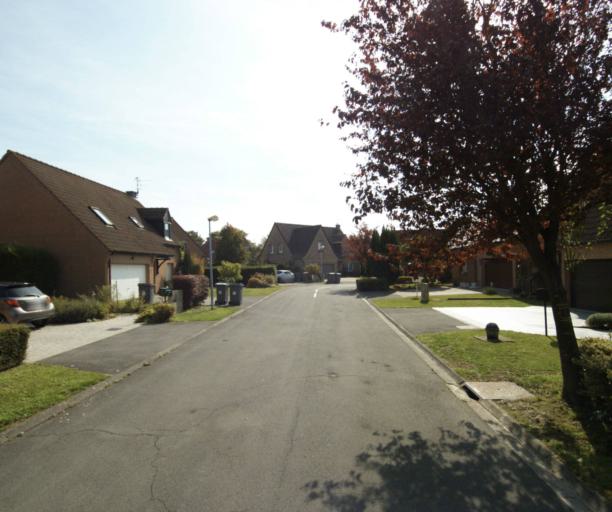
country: FR
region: Nord-Pas-de-Calais
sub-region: Departement du Nord
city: Capinghem
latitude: 50.6480
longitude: 2.9614
